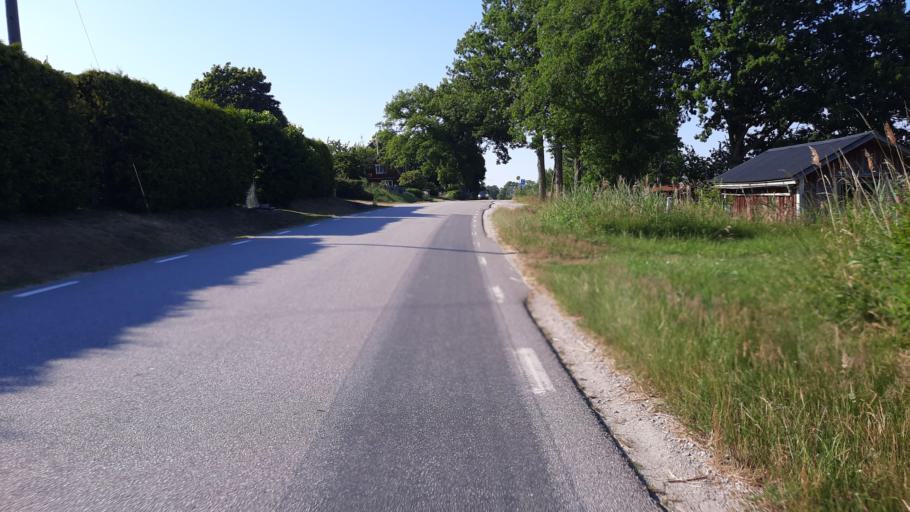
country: SE
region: Blekinge
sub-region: Karlskrona Kommun
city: Sturko
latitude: 56.1006
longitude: 15.6916
